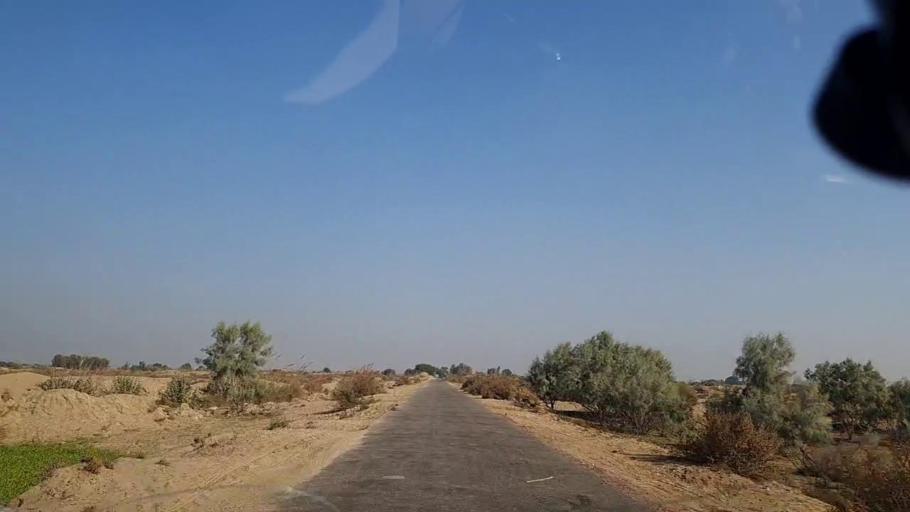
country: PK
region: Sindh
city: Khanpur
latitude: 27.6879
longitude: 69.5082
